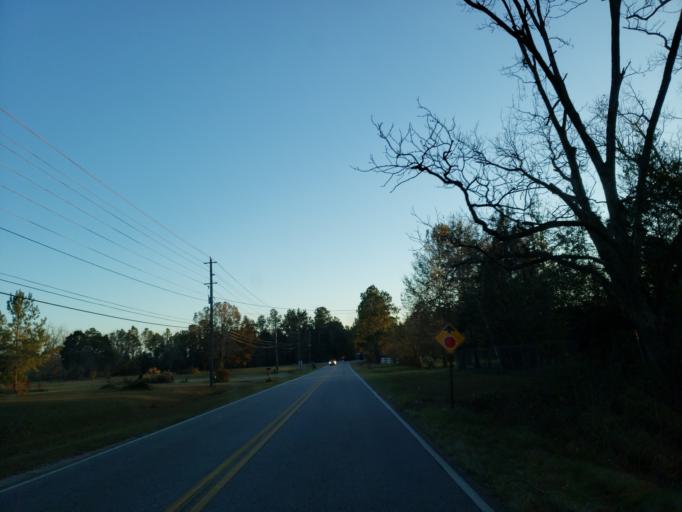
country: US
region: Georgia
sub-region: Crisp County
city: Cordele
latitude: 31.9287
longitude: -83.7663
